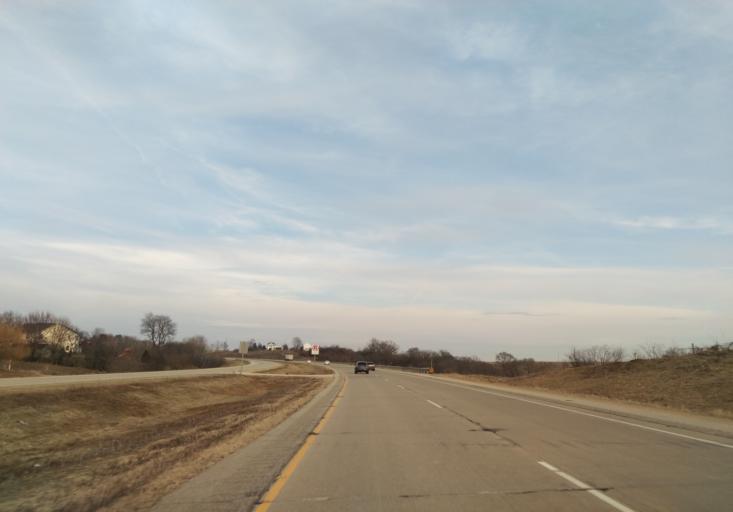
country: US
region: Wisconsin
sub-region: Dane County
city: Mount Horeb
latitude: 42.9928
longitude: -89.7404
